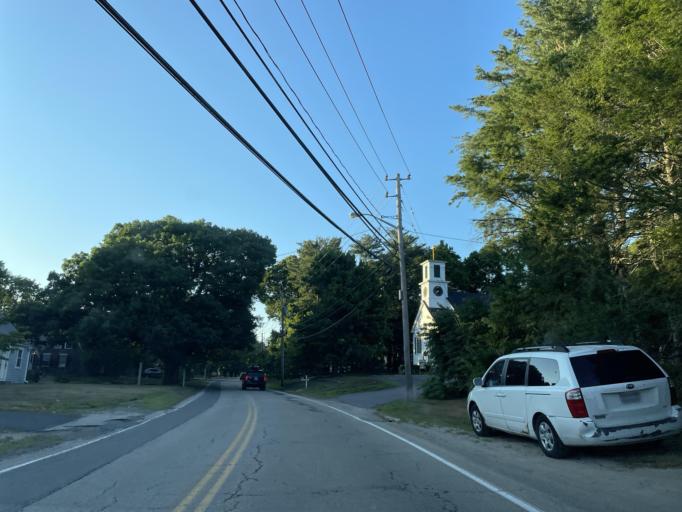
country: US
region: Massachusetts
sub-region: Plymouth County
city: Hanson
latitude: 42.0451
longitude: -70.8410
